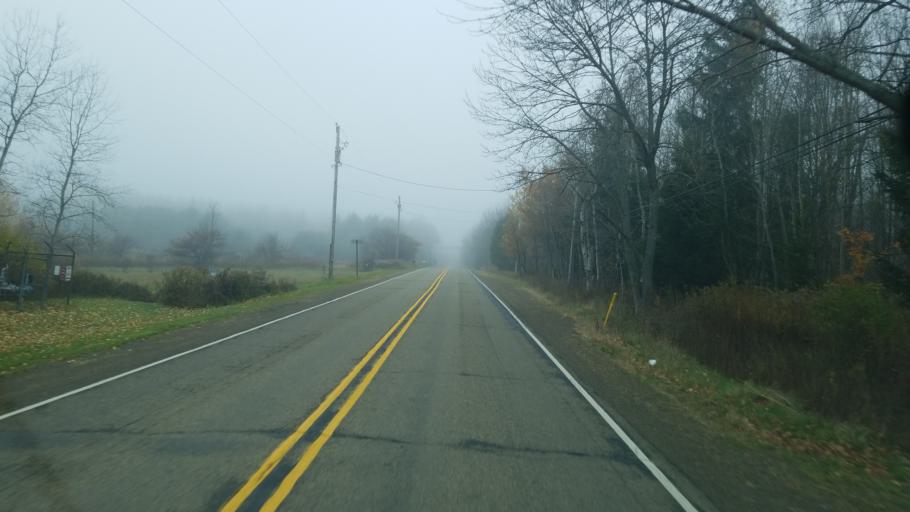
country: US
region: Pennsylvania
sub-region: McKean County
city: Smethport
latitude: 41.8112
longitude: -78.5457
